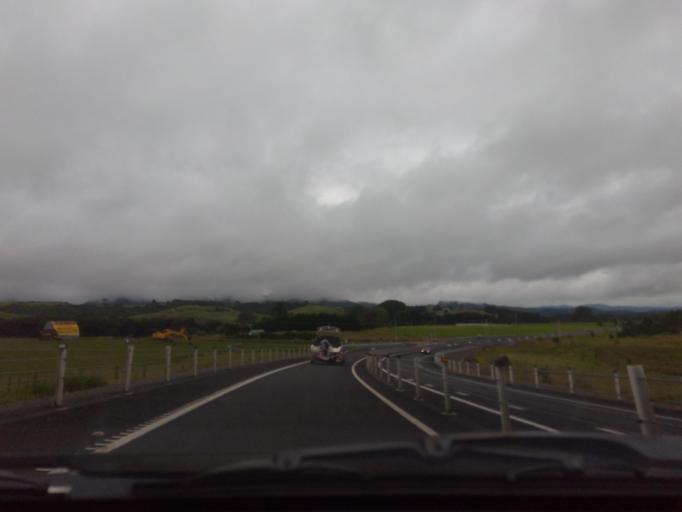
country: NZ
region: Northland
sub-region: Whangarei
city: Ruakaka
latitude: -36.0349
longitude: 174.4156
